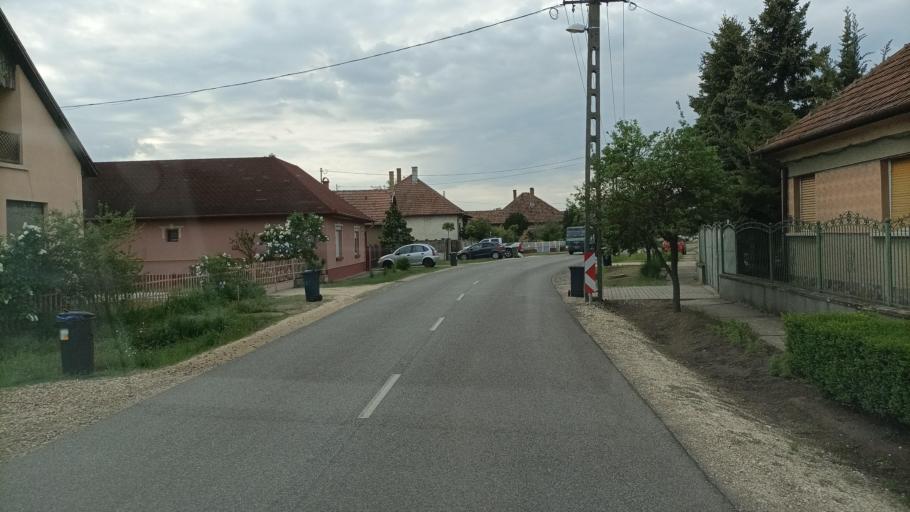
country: HU
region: Pest
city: Monor
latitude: 47.3225
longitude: 19.4071
